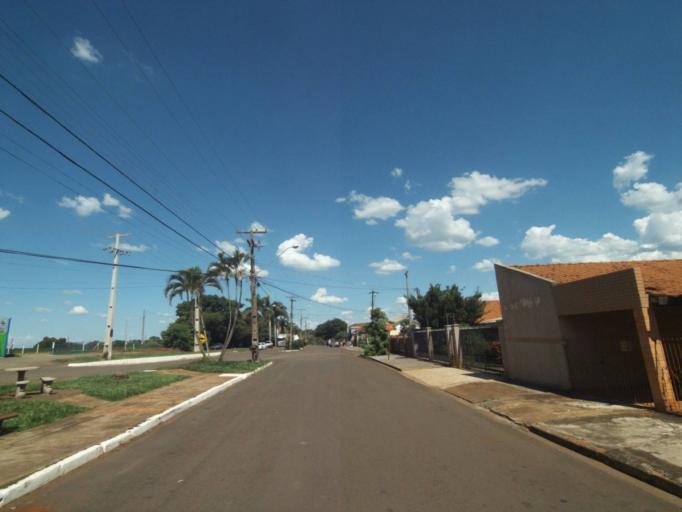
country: BR
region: Parana
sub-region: Sertanopolis
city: Sertanopolis
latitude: -23.0333
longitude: -50.8212
